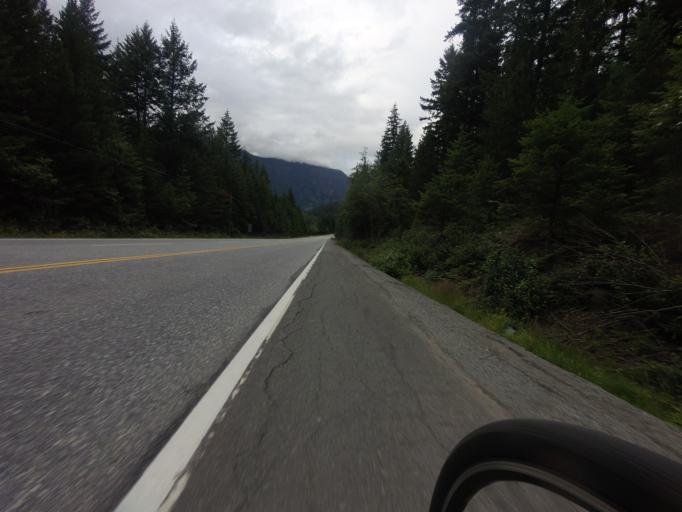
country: CA
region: British Columbia
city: Pemberton
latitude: 50.2472
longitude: -122.8624
